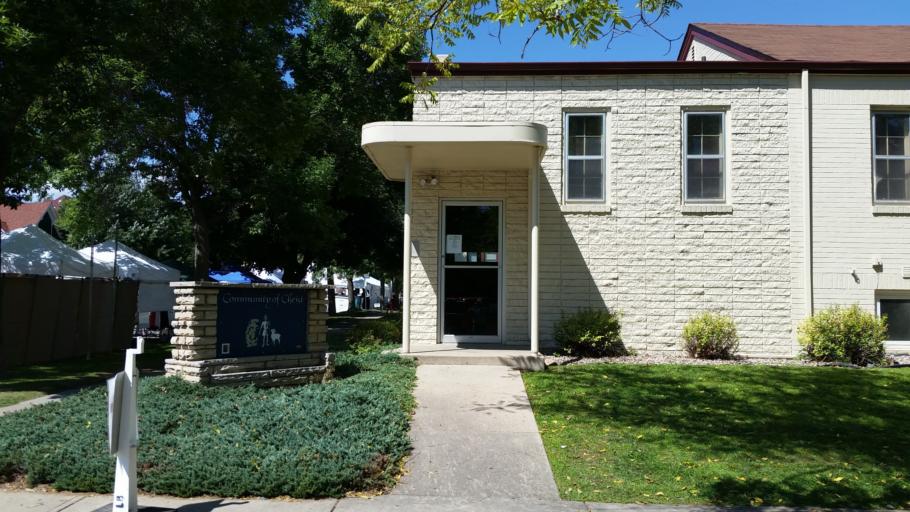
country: US
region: Colorado
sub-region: Larimer County
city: Fort Collins
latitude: 40.5857
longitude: -105.0742
